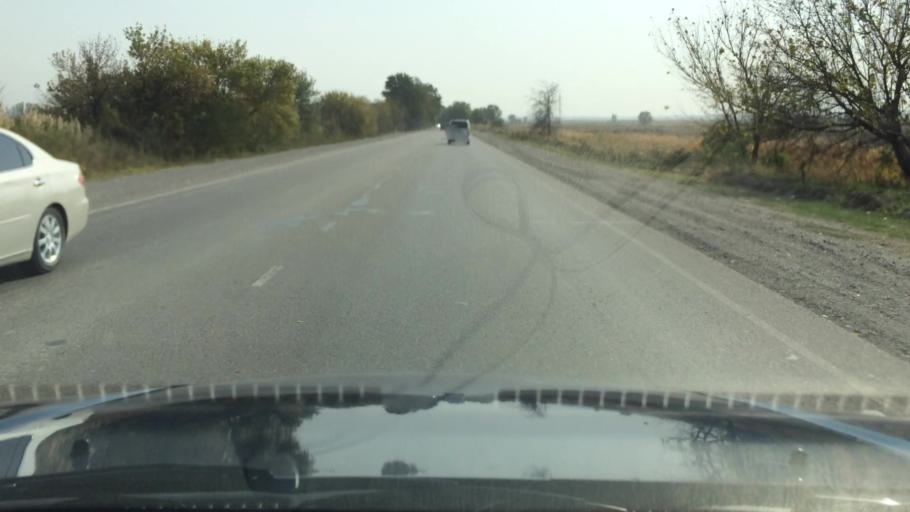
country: KG
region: Chuy
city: Lebedinovka
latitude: 42.9249
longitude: 74.7017
